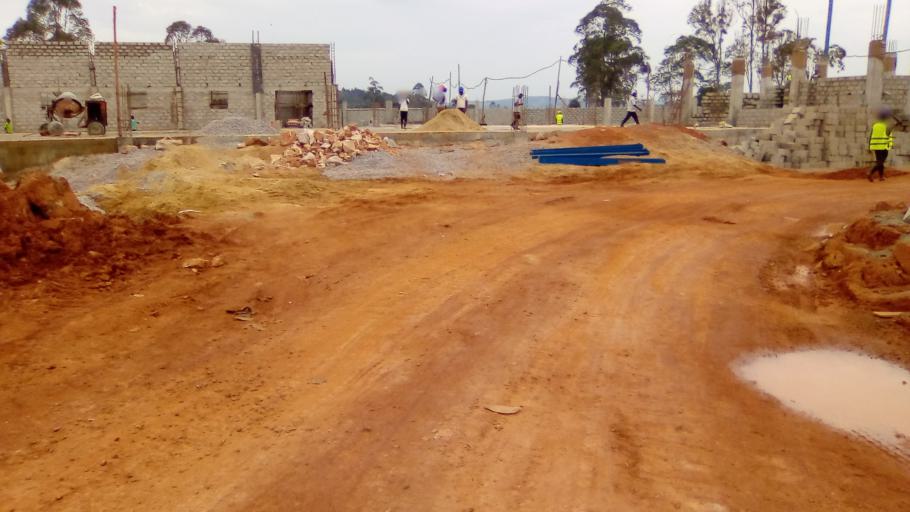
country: UG
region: Central Region
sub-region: Wakiso District
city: Kajansi
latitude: 0.1667
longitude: 32.5114
